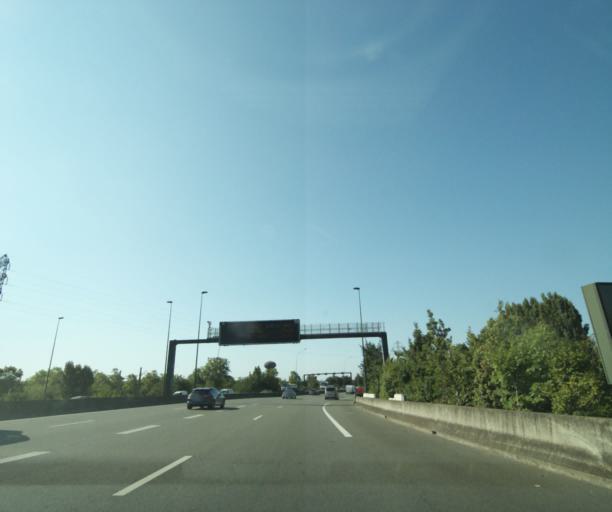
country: FR
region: Midi-Pyrenees
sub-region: Departement de la Haute-Garonne
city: Portet-sur-Garonne
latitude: 43.5645
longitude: 1.4183
